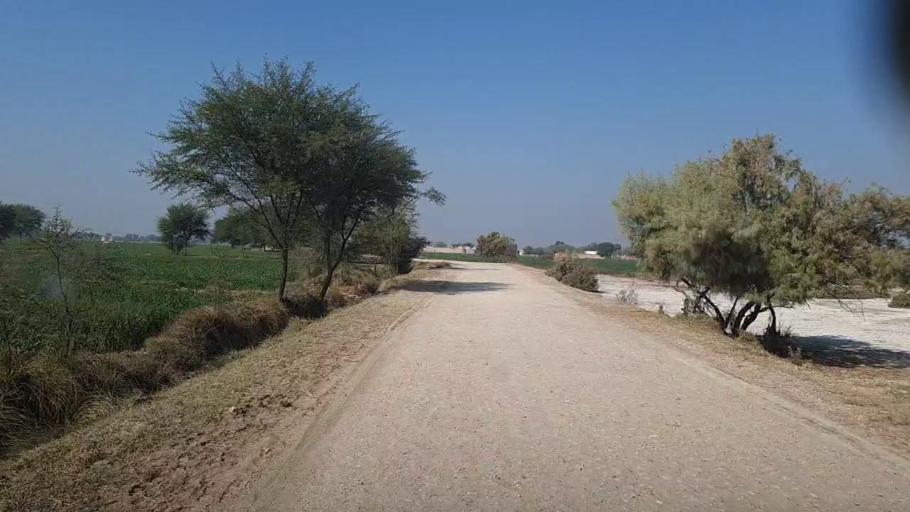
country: PK
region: Sindh
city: Khairpur
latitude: 27.9828
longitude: 69.6906
